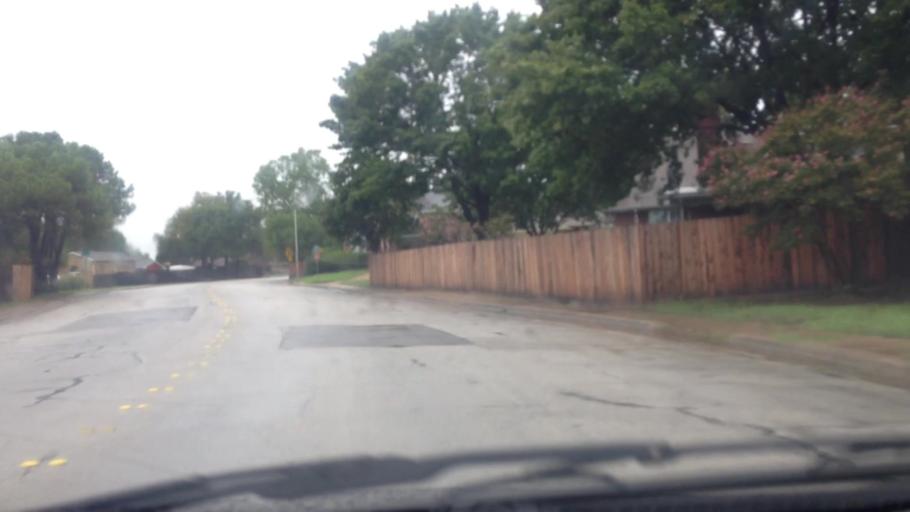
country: US
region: Texas
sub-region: Tarrant County
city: North Richland Hills
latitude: 32.8644
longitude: -97.2184
